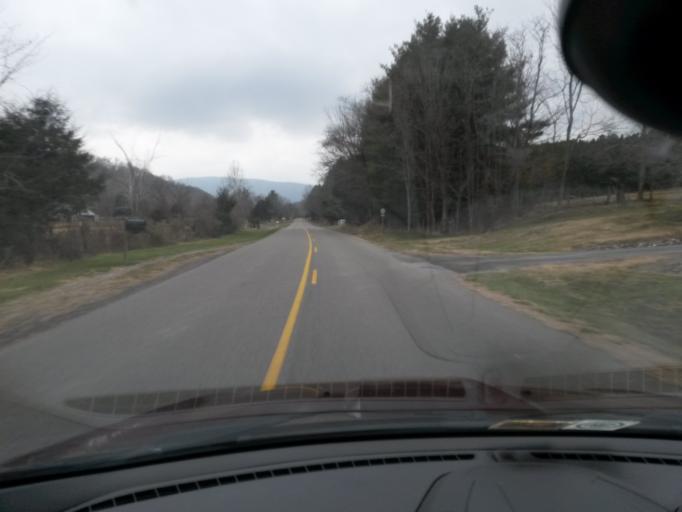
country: US
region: Virginia
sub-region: City of Lexington
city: Lexington
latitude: 37.8582
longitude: -79.5023
